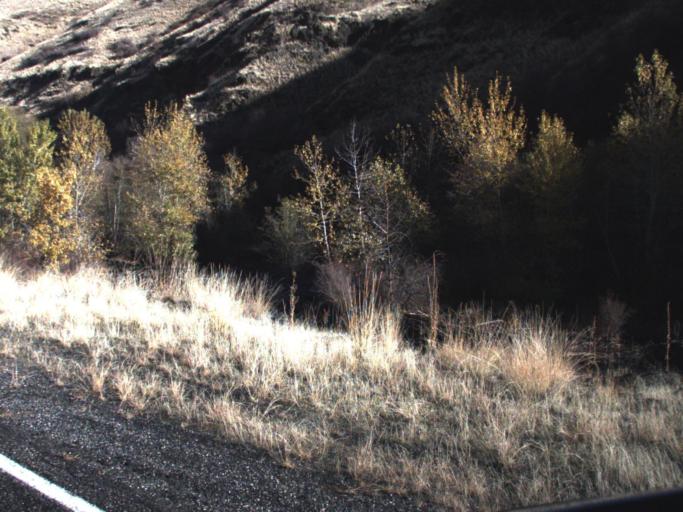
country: US
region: Washington
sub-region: Asotin County
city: Asotin
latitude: 46.0246
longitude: -117.2603
